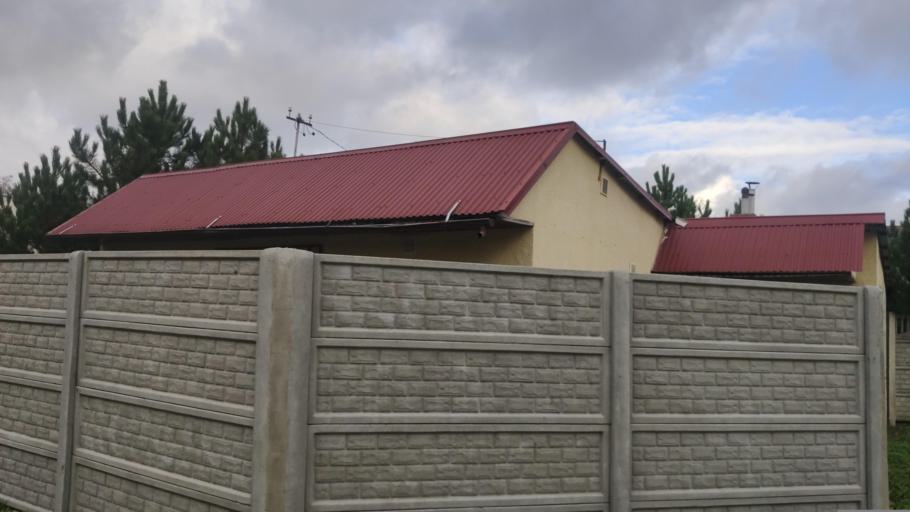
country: PL
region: Kujawsko-Pomorskie
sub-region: Powiat inowroclawski
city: Pakosc
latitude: 52.8191
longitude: 18.0386
